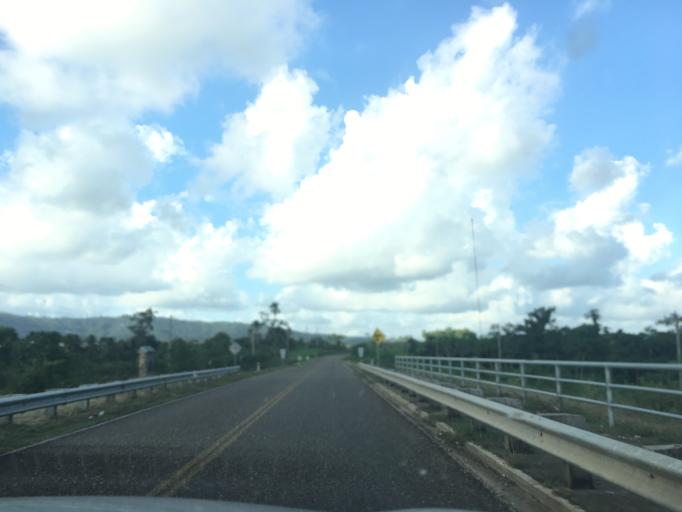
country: BZ
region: Stann Creek
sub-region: Dangriga
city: Dangriga
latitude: 16.8156
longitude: -88.3782
